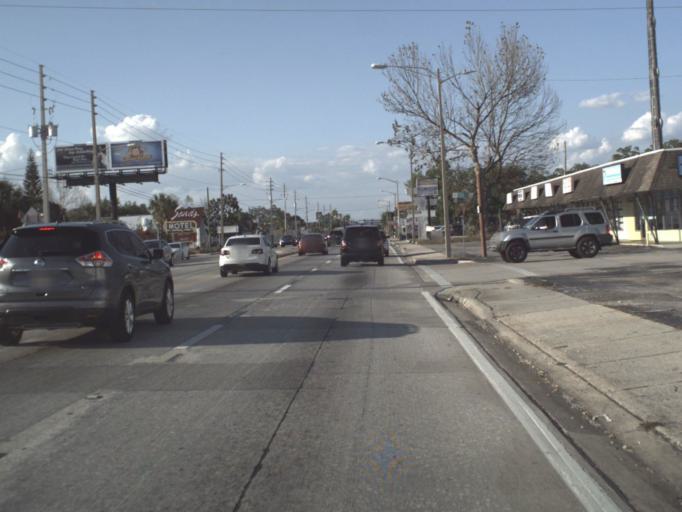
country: US
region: Florida
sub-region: Orange County
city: Holden Heights
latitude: 28.5161
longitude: -81.3969
